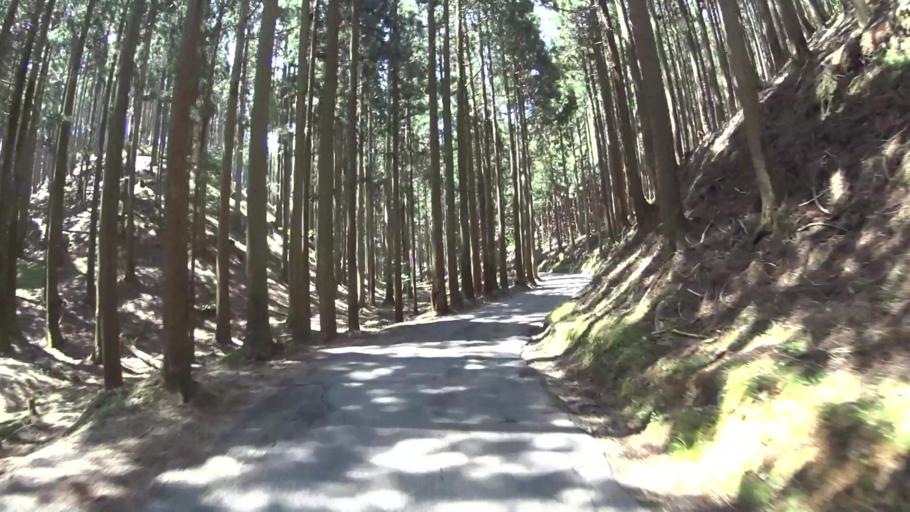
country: JP
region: Shiga Prefecture
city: Kitahama
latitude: 35.1557
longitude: 135.7994
